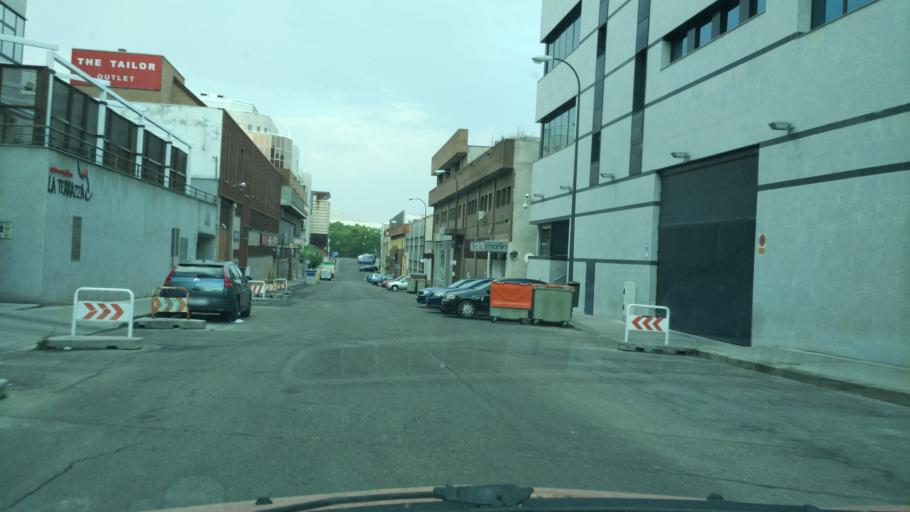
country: ES
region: Madrid
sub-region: Provincia de Madrid
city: Pinar de Chamartin
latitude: 40.4895
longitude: -3.6917
